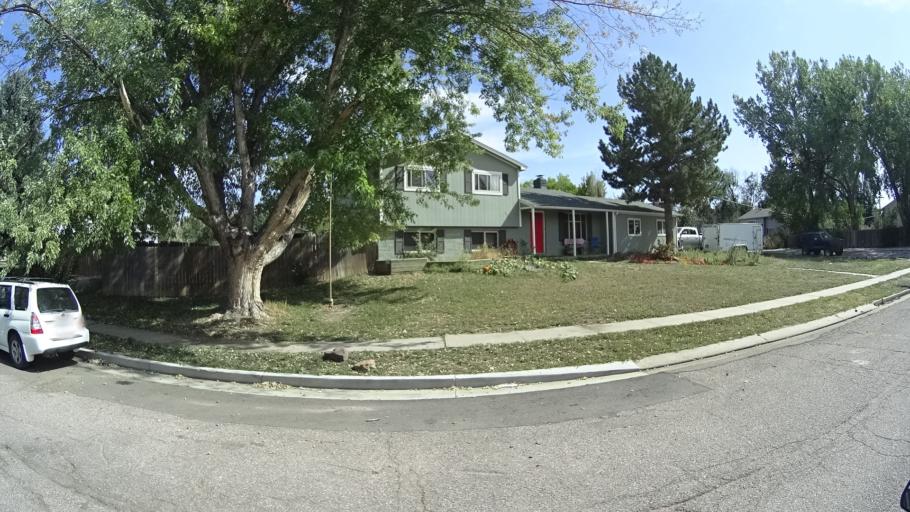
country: US
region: Colorado
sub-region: El Paso County
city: Colorado Springs
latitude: 38.8917
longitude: -104.7703
